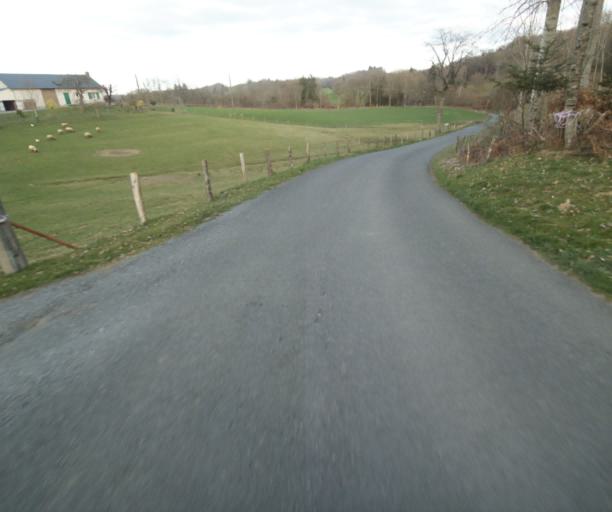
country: FR
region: Limousin
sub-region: Departement de la Correze
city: Uzerche
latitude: 45.3626
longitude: 1.6098
